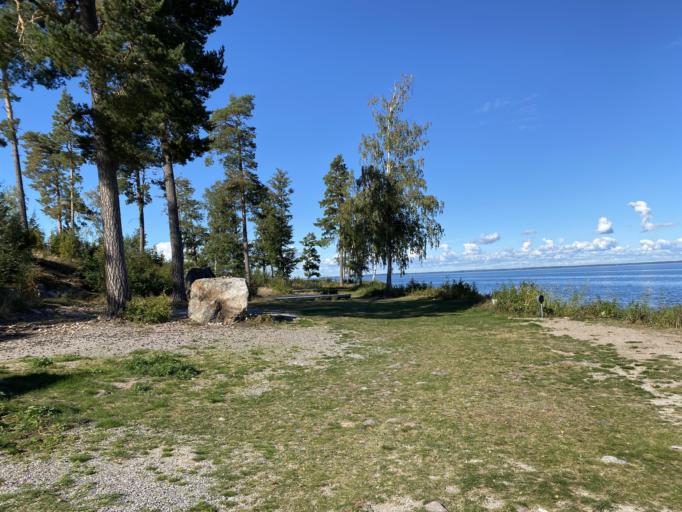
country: SE
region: Soedermanland
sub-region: Vingakers Kommun
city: Vingaker
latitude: 59.1876
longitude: 15.8943
